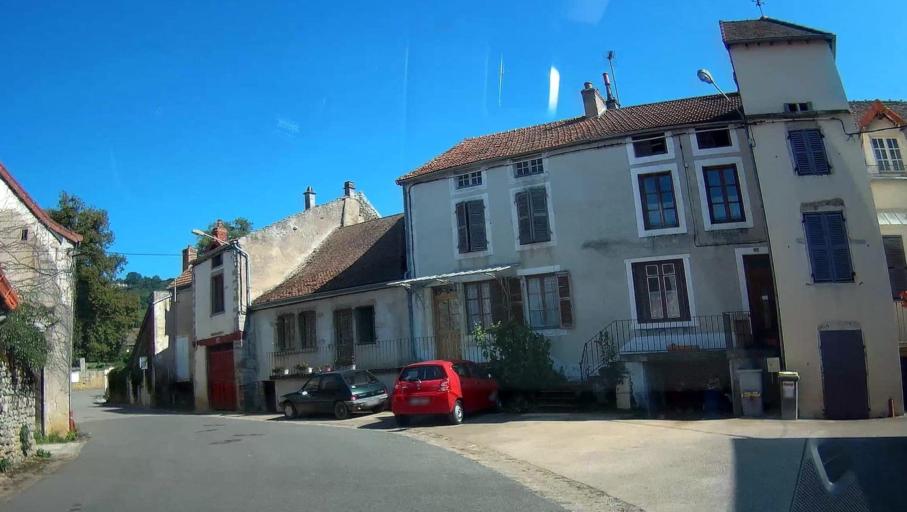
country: FR
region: Bourgogne
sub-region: Departement de la Cote-d'Or
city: Nolay
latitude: 46.9541
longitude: 4.6361
